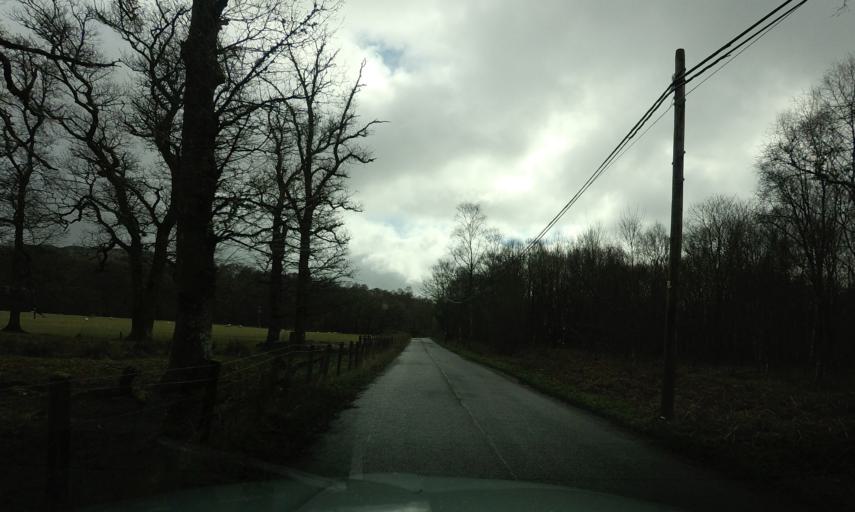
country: GB
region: Scotland
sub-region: West Dunbartonshire
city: Balloch
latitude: 56.1035
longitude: -4.5659
